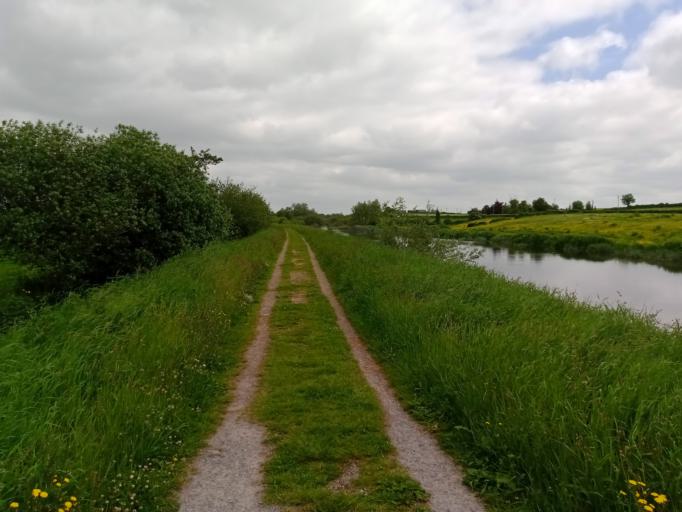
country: IE
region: Leinster
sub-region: County Carlow
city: Bagenalstown
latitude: 52.7489
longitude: -6.9681
